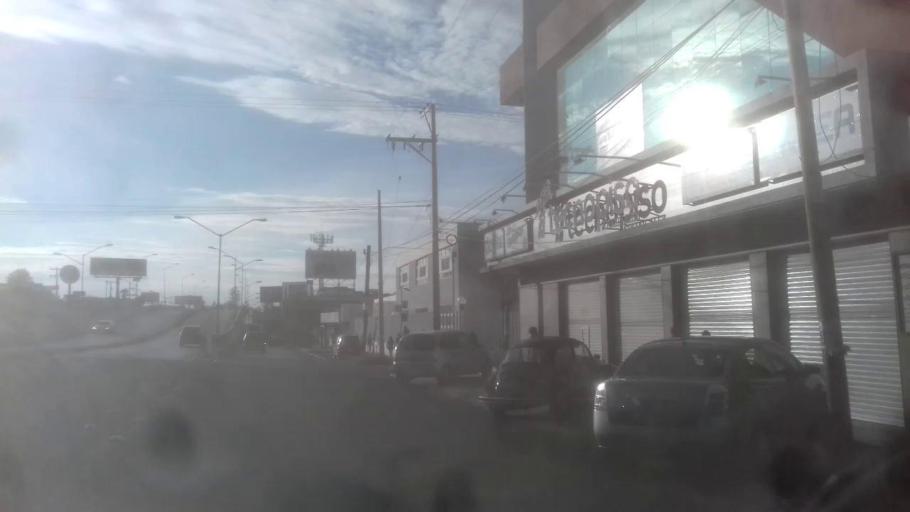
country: MX
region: Aguascalientes
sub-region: Aguascalientes
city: Aguascalientes
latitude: 21.8658
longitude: -102.2974
